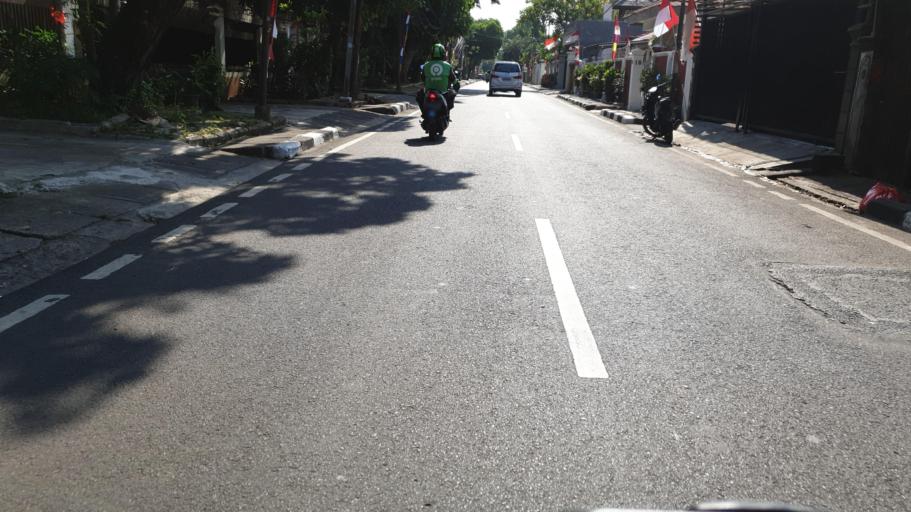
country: ID
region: Jakarta Raya
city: Jakarta
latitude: -6.2875
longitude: 106.8424
